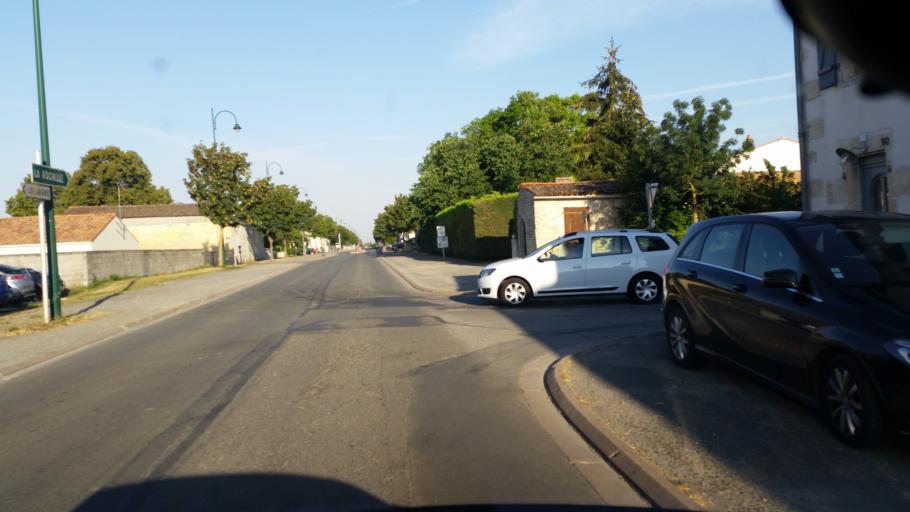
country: FR
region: Poitou-Charentes
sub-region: Departement de la Charente-Maritime
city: Saint-Jean-de-Liversay
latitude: 46.2273
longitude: -0.8611
